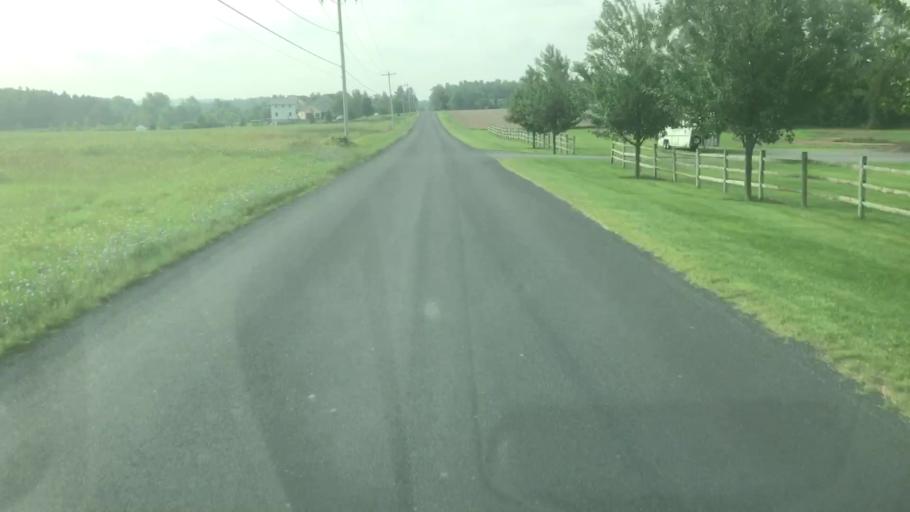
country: US
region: New York
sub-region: Onondaga County
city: Skaneateles
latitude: 42.9270
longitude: -76.4572
